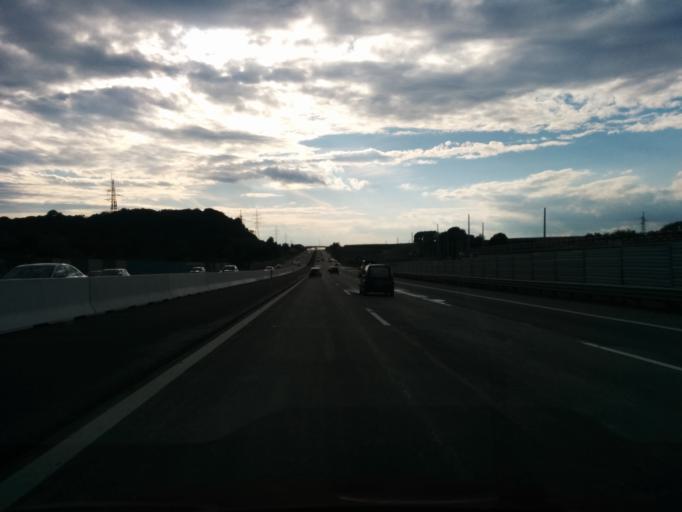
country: AT
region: Lower Austria
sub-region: Sankt Polten Stadt
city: Sankt Poelten
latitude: 48.1770
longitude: 15.6130
